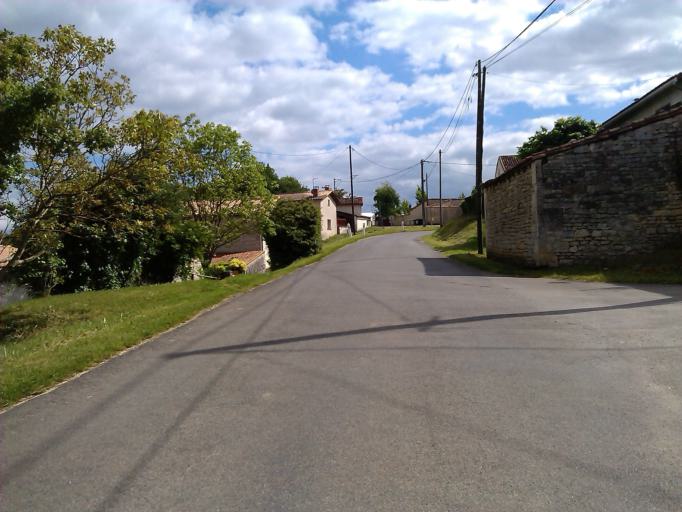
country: FR
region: Poitou-Charentes
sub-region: Departement de la Charente
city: Mansle
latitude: 45.9050
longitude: 0.2177
